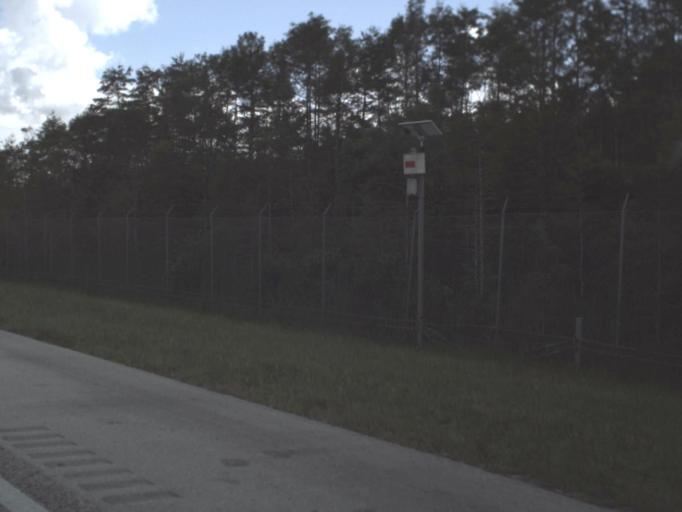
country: US
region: Florida
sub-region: Collier County
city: Immokalee
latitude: 26.1680
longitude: -81.1085
